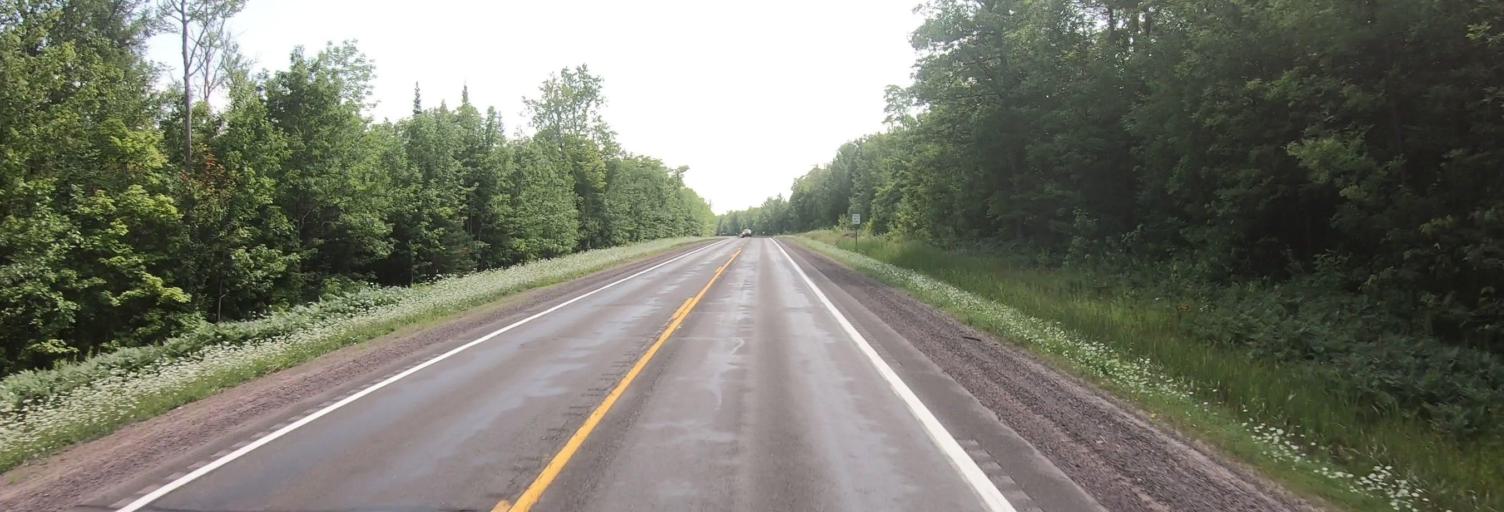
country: US
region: Michigan
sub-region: Ontonagon County
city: Ontonagon
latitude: 46.8328
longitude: -88.9949
